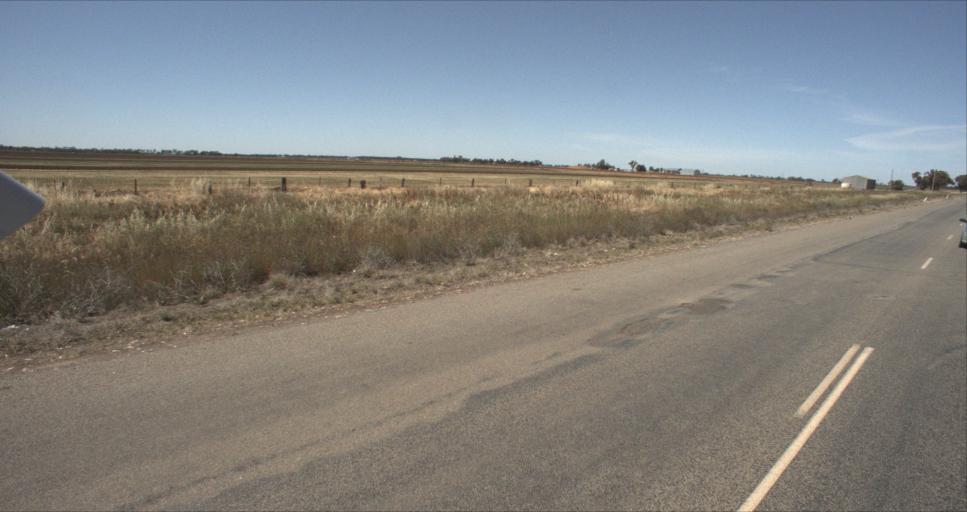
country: AU
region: New South Wales
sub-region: Leeton
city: Leeton
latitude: -34.4978
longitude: 146.2875
